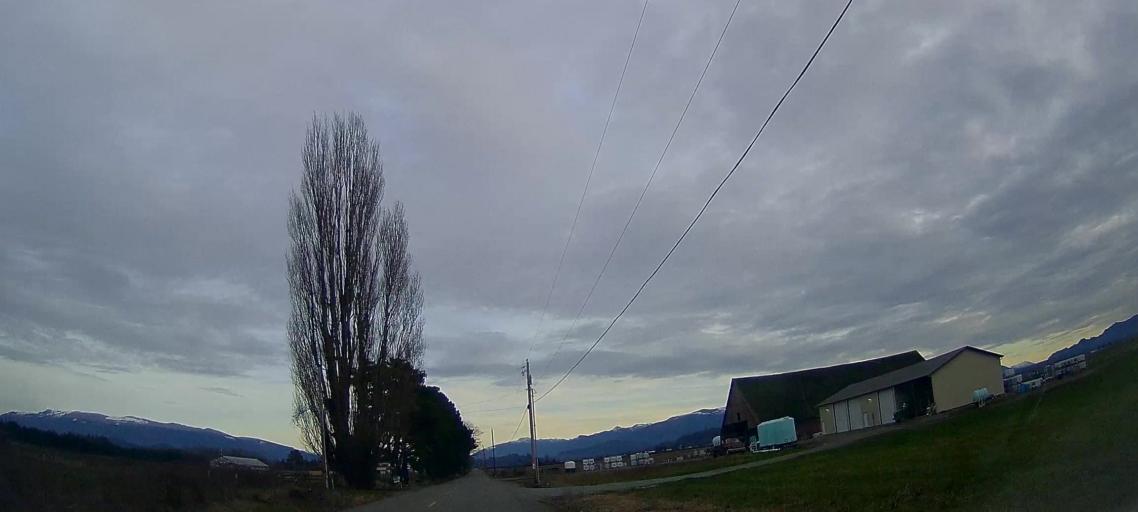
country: US
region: Washington
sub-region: Skagit County
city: Burlington
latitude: 48.5013
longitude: -122.4007
